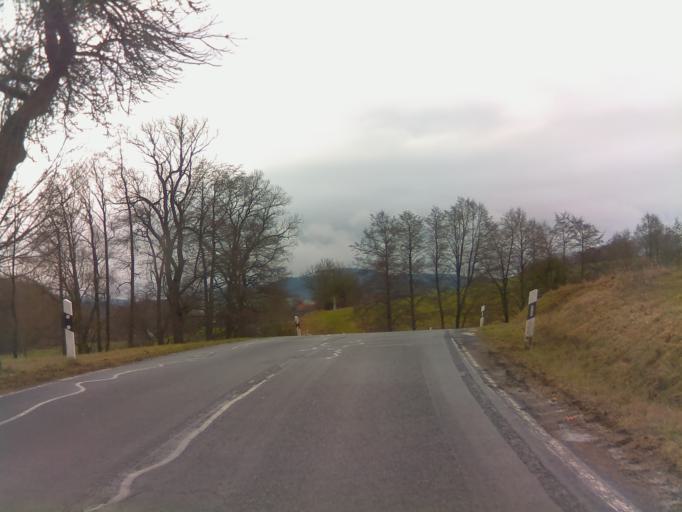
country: DE
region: Thuringia
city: Geisa
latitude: 50.6925
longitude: 9.9300
